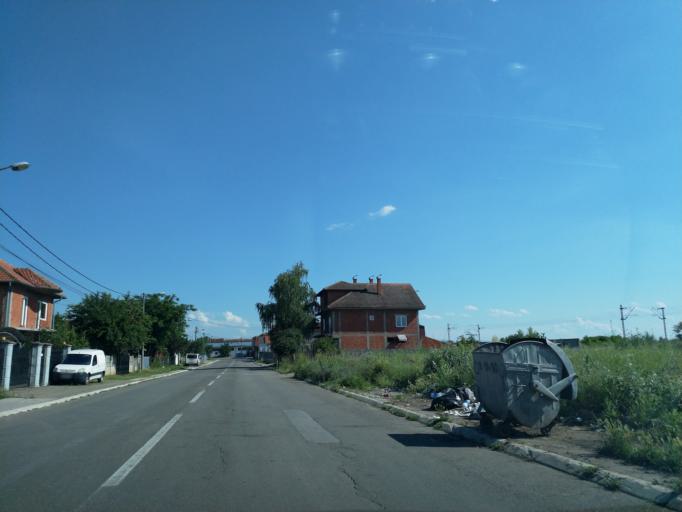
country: RS
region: Central Serbia
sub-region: Pomoravski Okrug
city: Paracin
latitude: 43.8489
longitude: 21.4119
